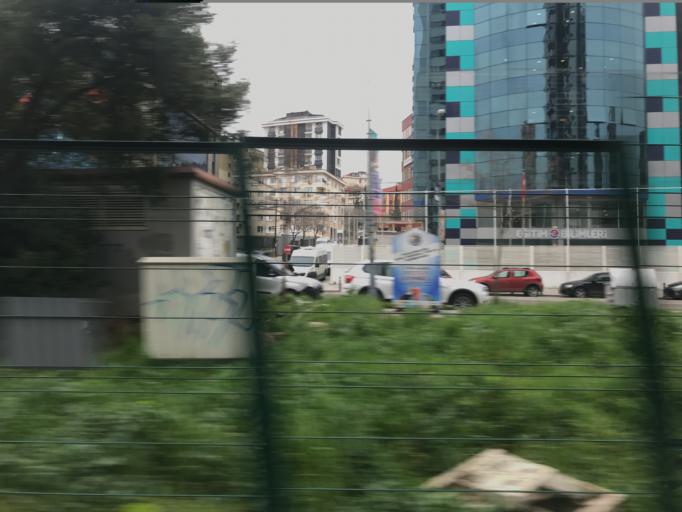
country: TR
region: Istanbul
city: Maltepe
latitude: 40.8965
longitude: 29.1728
